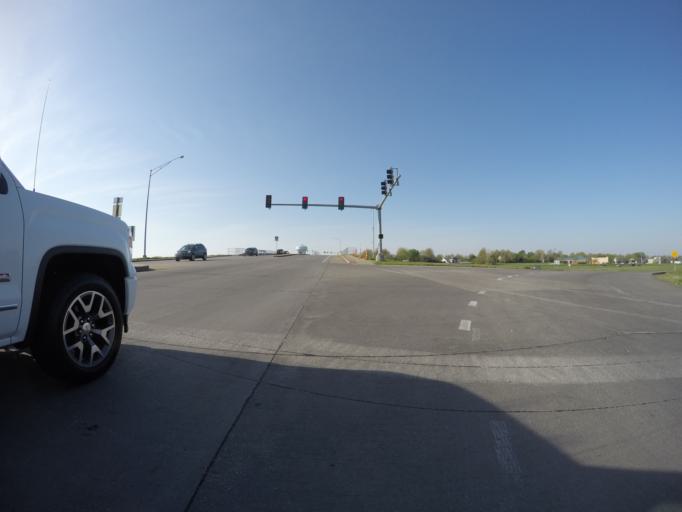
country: US
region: Missouri
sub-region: Jackson County
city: Lees Summit
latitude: 38.9033
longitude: -94.3399
